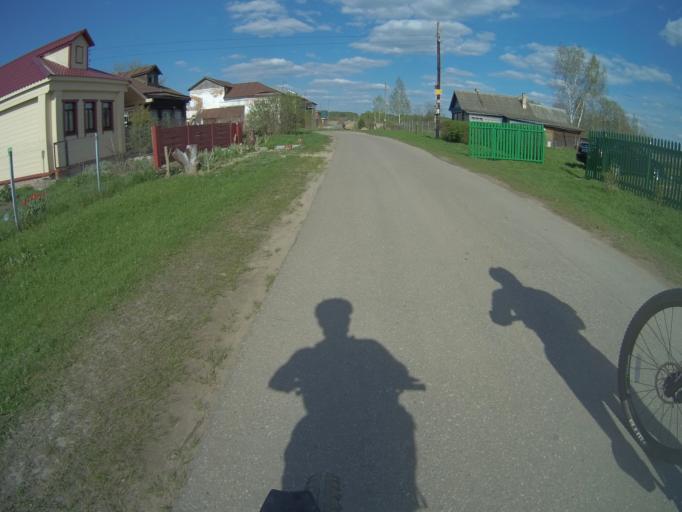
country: RU
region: Vladimir
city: Vorsha
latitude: 56.0092
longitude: 40.1524
